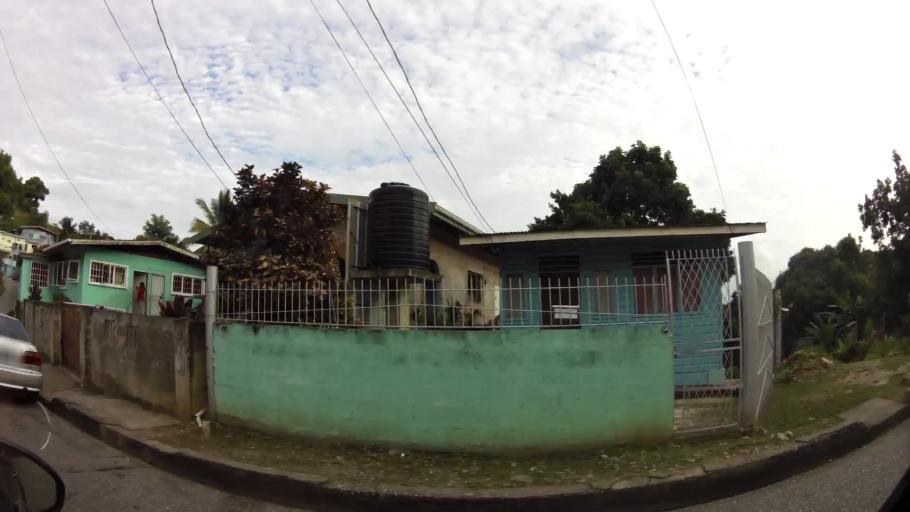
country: TT
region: San Juan/Laventille
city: Laventille
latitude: 10.6621
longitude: -61.4886
